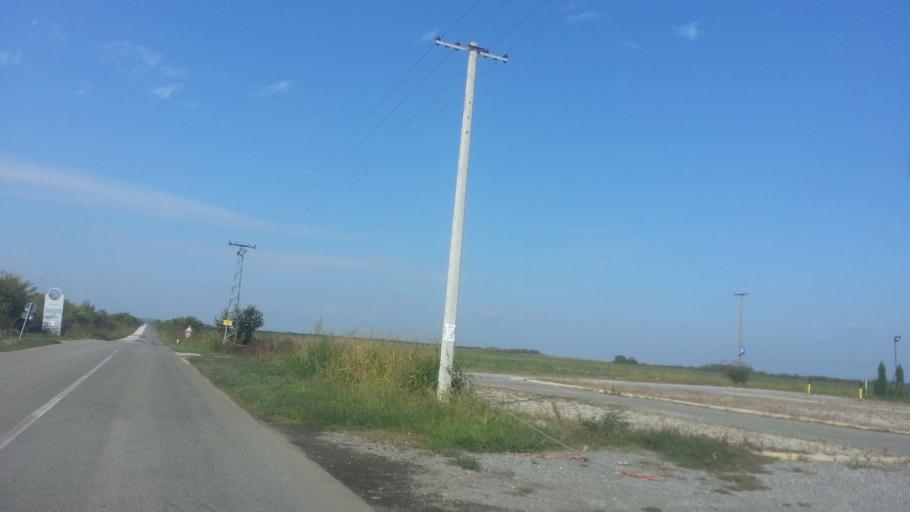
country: RS
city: Surduk
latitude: 45.0993
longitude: 20.2904
